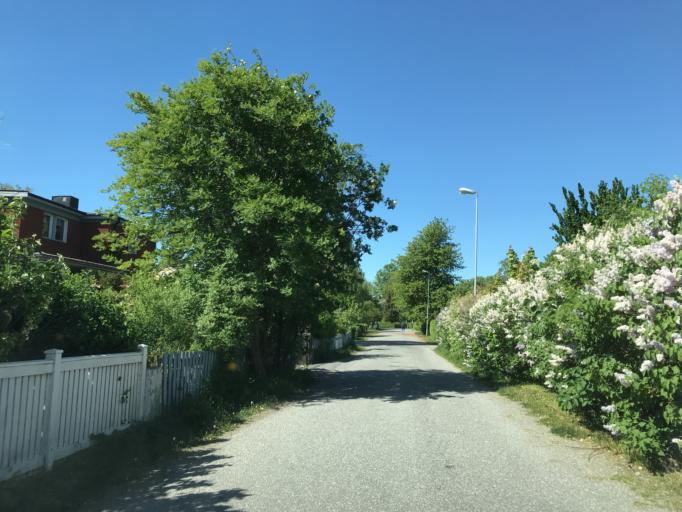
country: SE
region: Stockholm
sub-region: Sollentuna Kommun
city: Sollentuna
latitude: 59.4206
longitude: 17.9629
